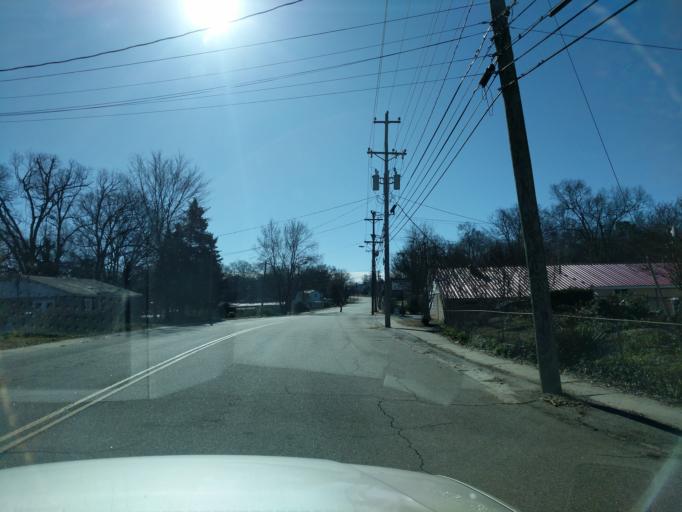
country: US
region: South Carolina
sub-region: Laurens County
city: Clinton
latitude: 34.4863
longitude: -81.8820
